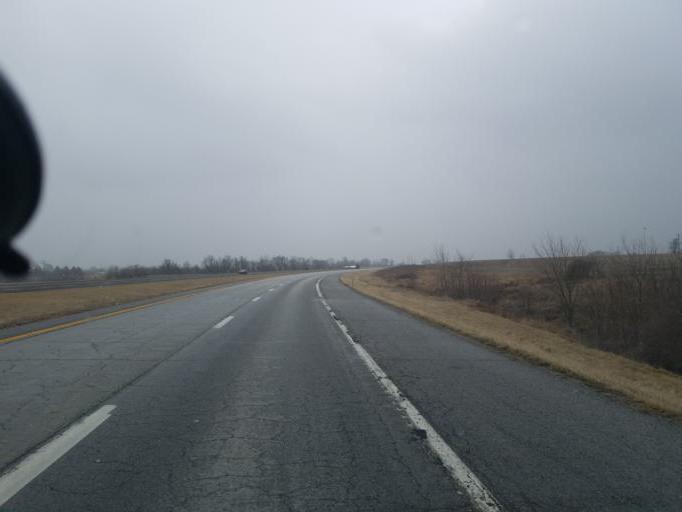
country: US
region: Missouri
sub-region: Macon County
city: La Plata
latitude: 40.0174
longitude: -92.4759
